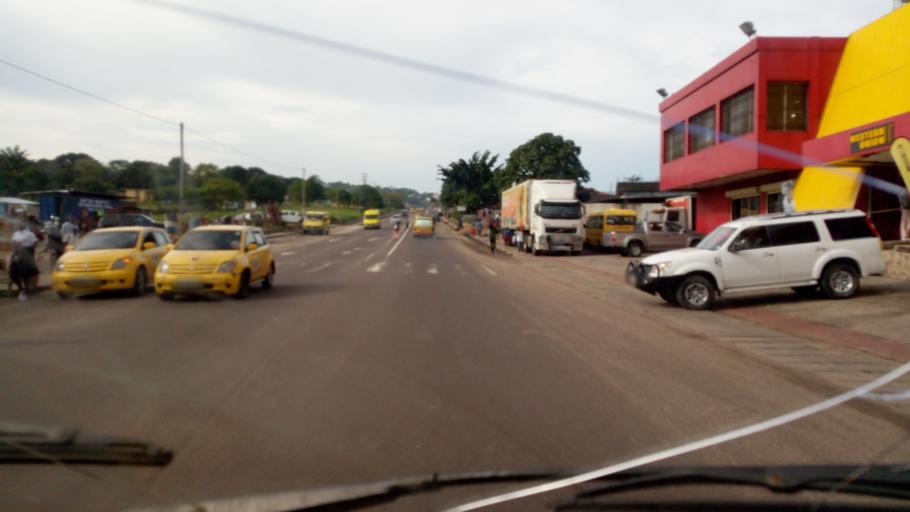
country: CD
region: Kinshasa
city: Kinshasa
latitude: -4.4337
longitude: 15.2580
